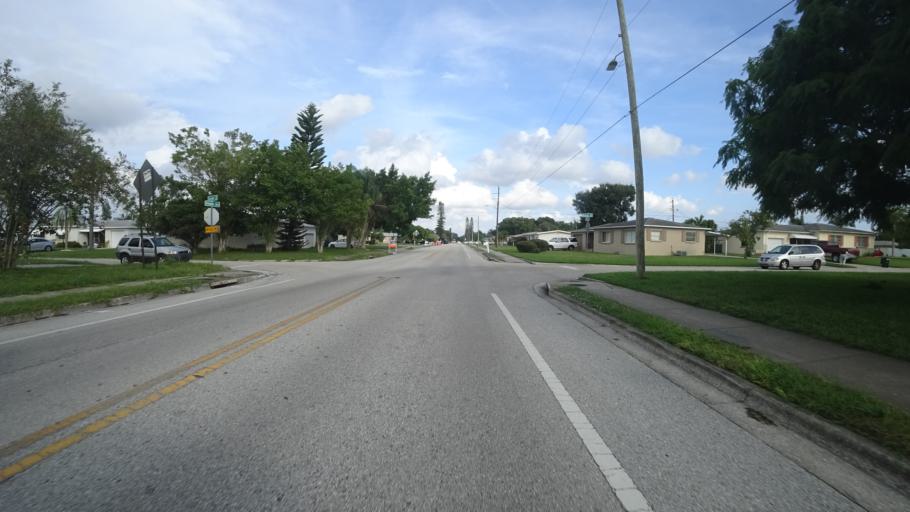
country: US
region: Florida
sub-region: Manatee County
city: South Bradenton
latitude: 27.4583
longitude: -82.5731
